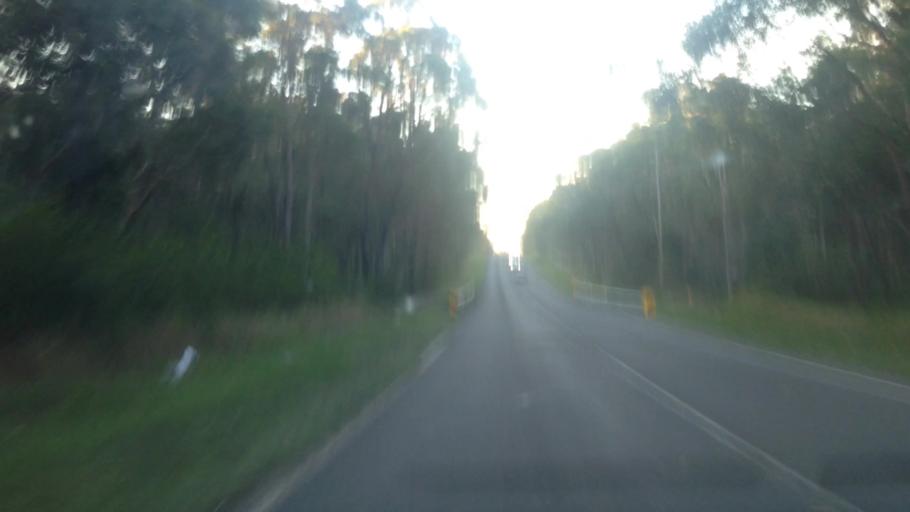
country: AU
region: New South Wales
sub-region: Lake Macquarie Shire
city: Dora Creek
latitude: -33.1466
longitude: 151.4790
